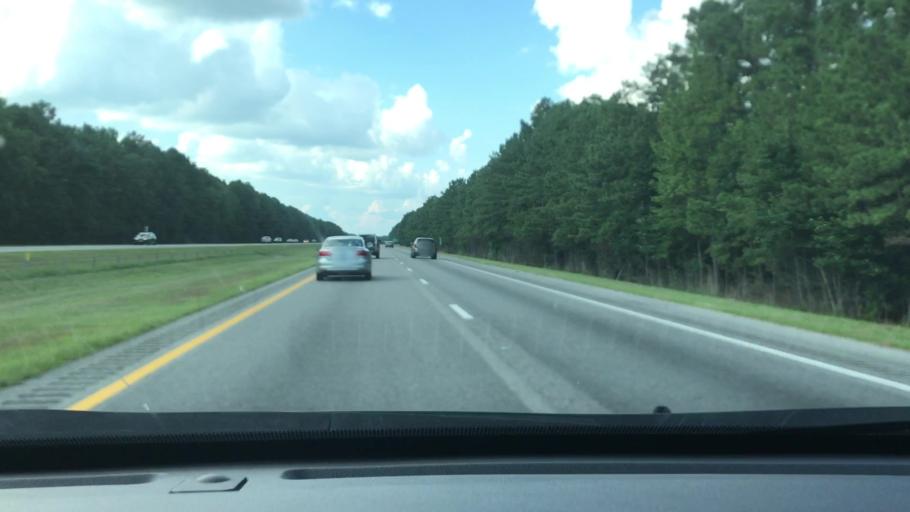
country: US
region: South Carolina
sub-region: Florence County
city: Timmonsville
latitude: 34.0138
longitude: -79.9970
